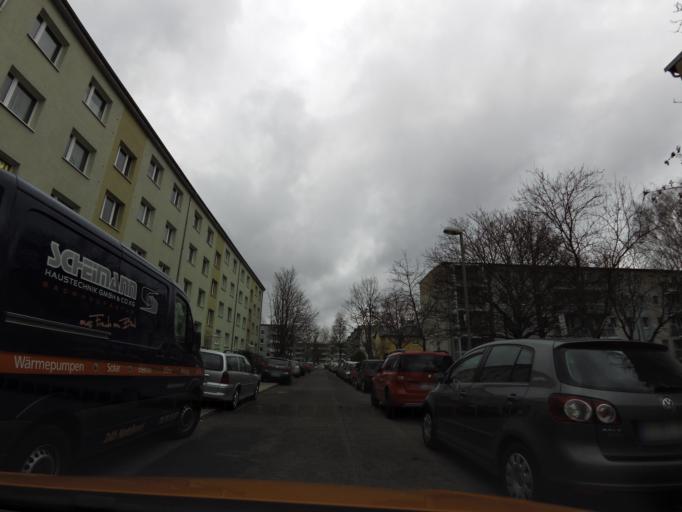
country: DE
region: Berlin
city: Lichtenberg
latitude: 52.5160
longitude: 13.5042
